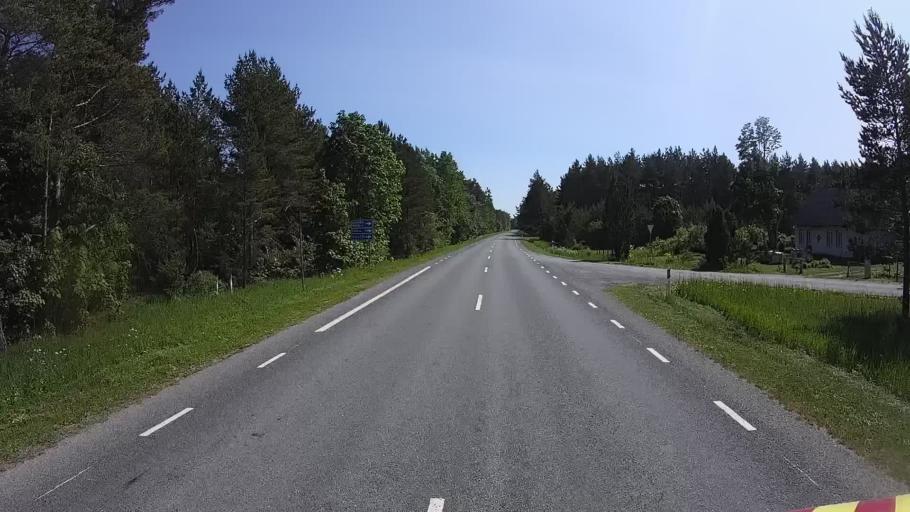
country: EE
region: Saare
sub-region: Kuressaare linn
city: Kuressaare
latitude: 58.3588
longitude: 22.4413
